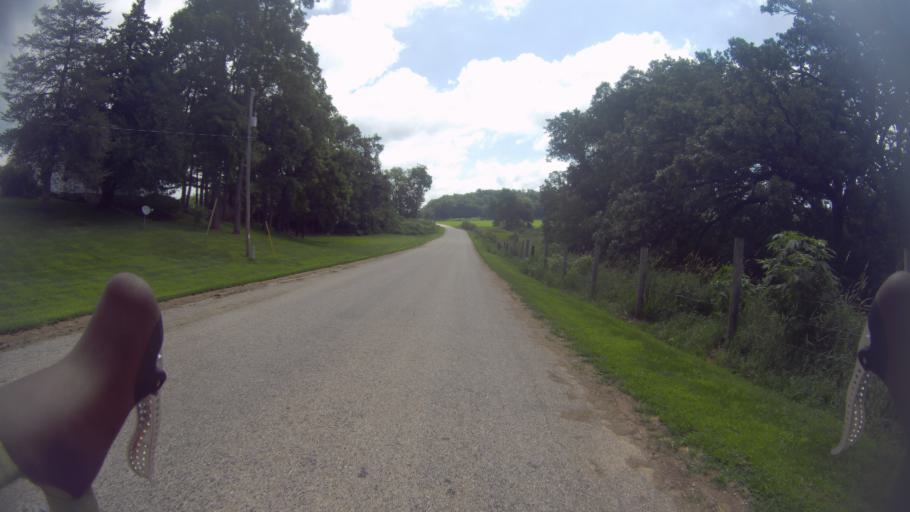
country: US
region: Wisconsin
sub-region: Sauk County
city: Sauk City
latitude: 43.2281
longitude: -89.6182
